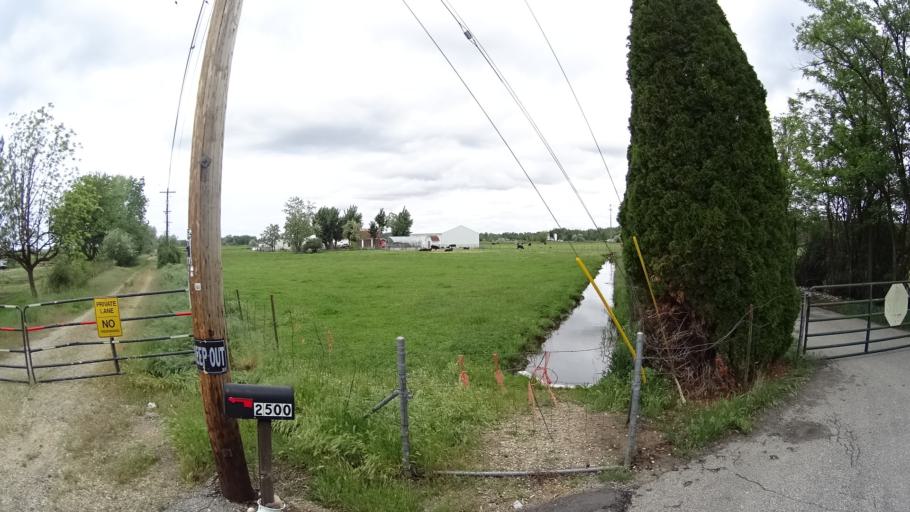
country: US
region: Idaho
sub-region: Ada County
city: Eagle
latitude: 43.6846
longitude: -116.3828
